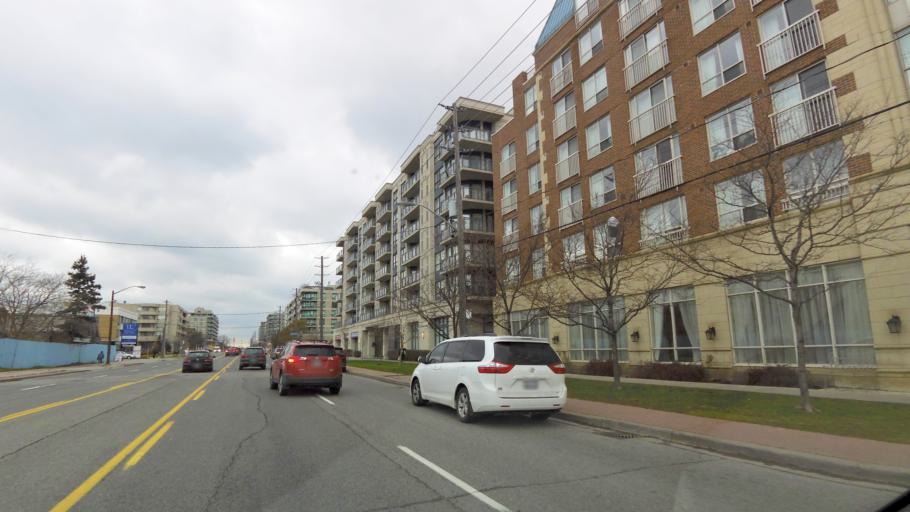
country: CA
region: Ontario
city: North York
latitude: 43.7523
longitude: -79.4537
